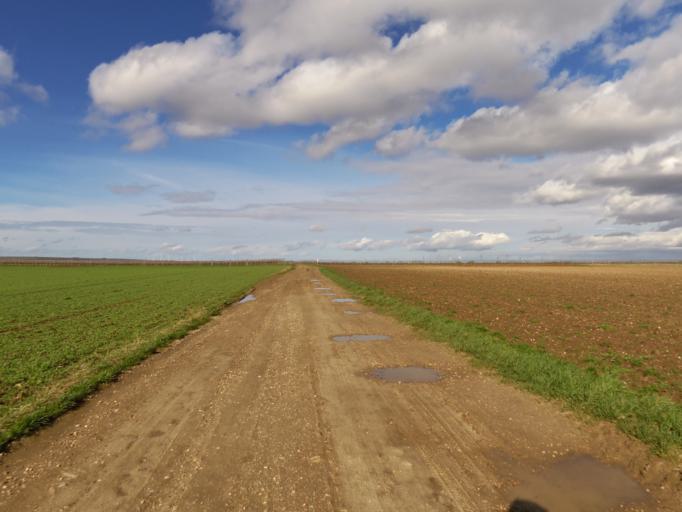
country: DE
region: Rheinland-Pfalz
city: Offstein
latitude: 49.5891
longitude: 8.2599
